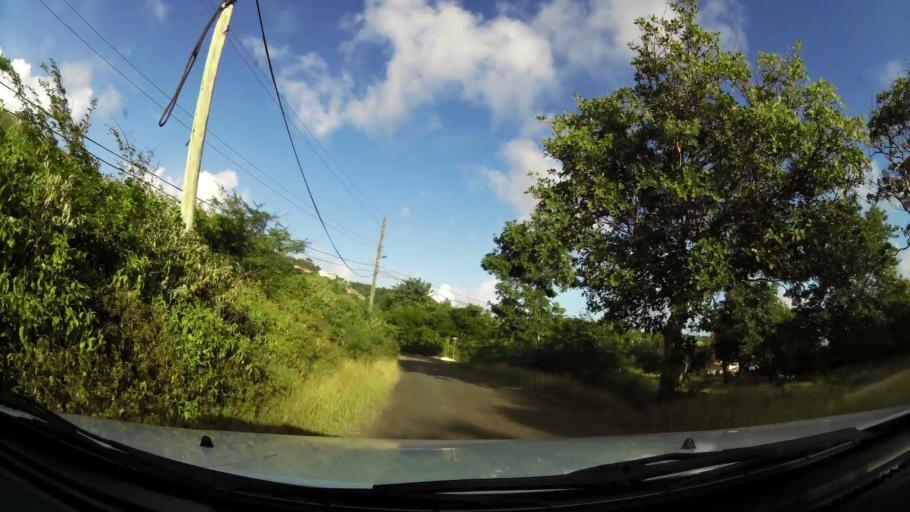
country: LC
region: Gros-Islet
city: Gros Islet
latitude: 14.0979
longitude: -60.9316
